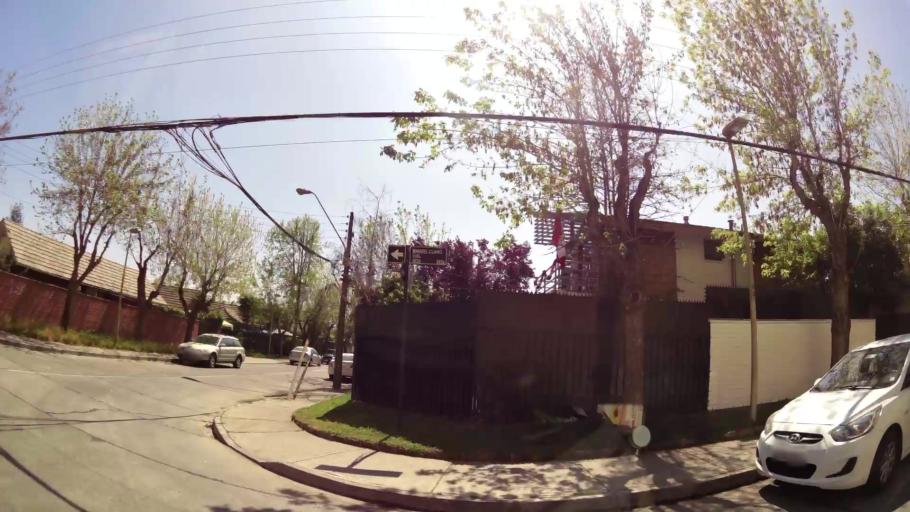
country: CL
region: Santiago Metropolitan
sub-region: Provincia de Santiago
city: Villa Presidente Frei, Nunoa, Santiago, Chile
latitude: -33.4274
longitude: -70.5409
